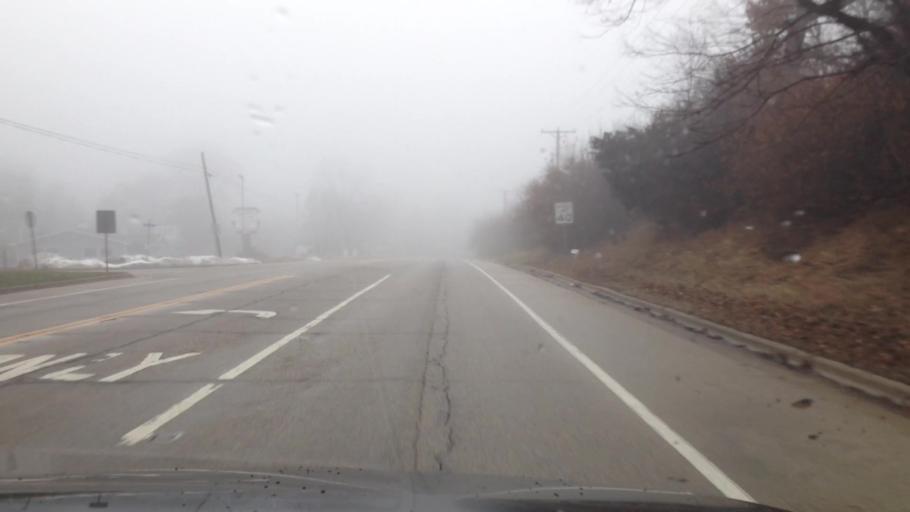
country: US
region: Illinois
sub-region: McHenry County
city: Hebron
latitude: 42.4775
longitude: -88.4369
